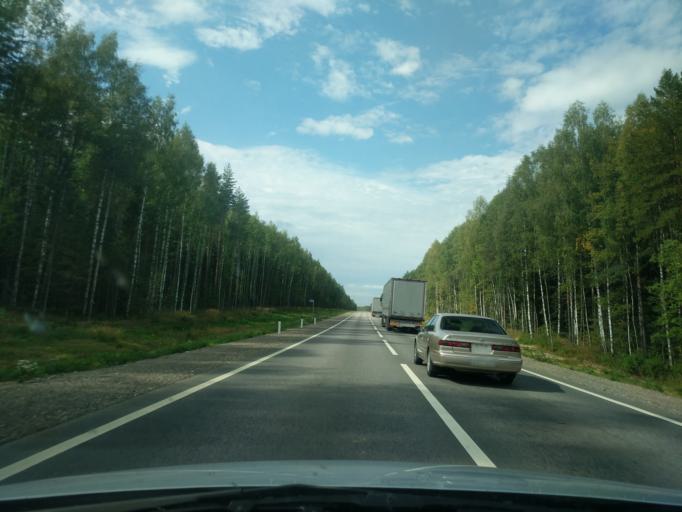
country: RU
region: Kostroma
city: Kadyy
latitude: 57.7981
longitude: 42.8333
